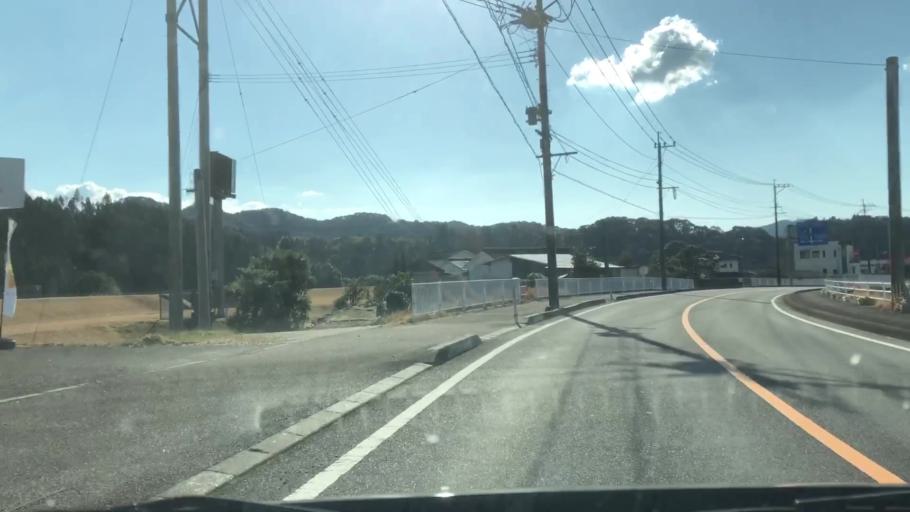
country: JP
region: Kagoshima
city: Satsumasendai
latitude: 31.8573
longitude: 130.3911
